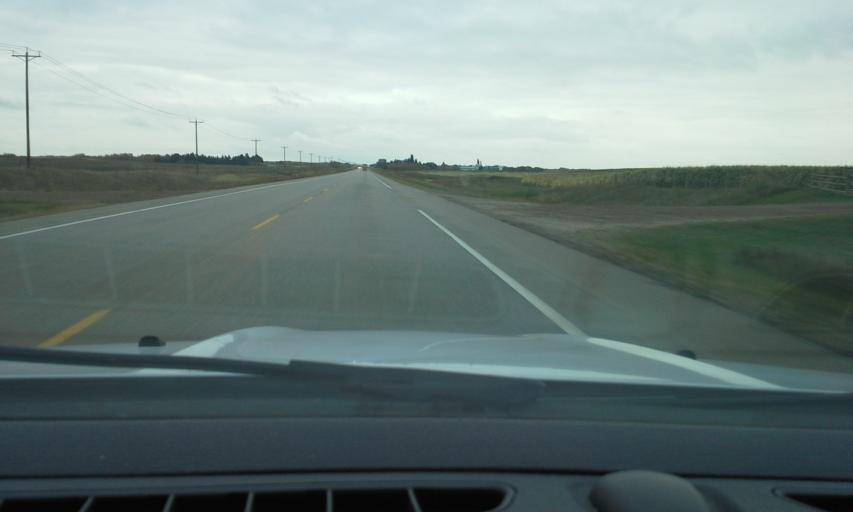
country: CA
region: Saskatchewan
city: Lloydminster
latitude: 53.2780
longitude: -109.8703
